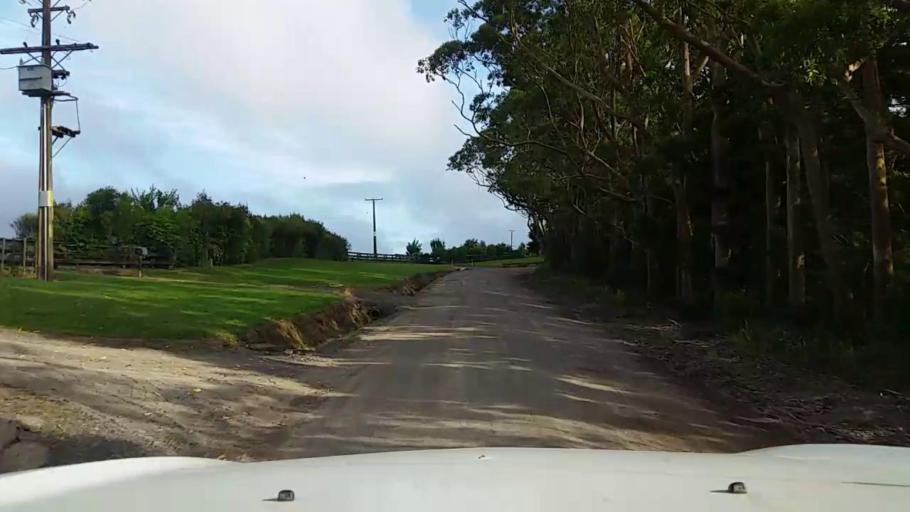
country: NZ
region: Northland
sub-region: Whangarei
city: Maungatapere
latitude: -35.6716
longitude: 174.1751
